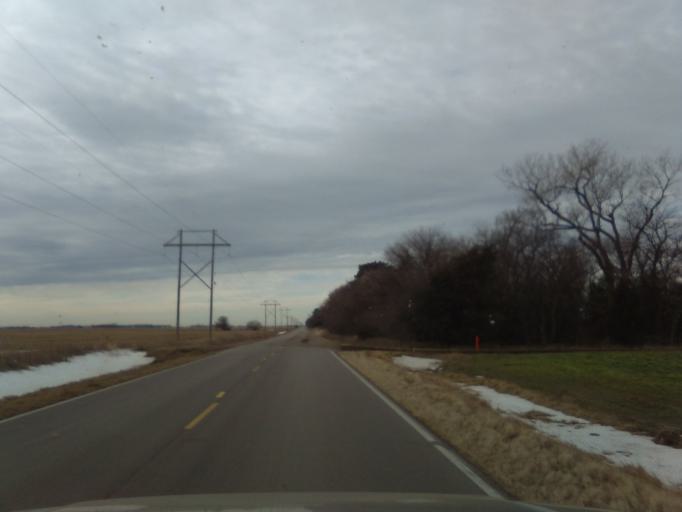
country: US
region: Nebraska
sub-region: Buffalo County
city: Gibbon
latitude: 40.6550
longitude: -98.8047
